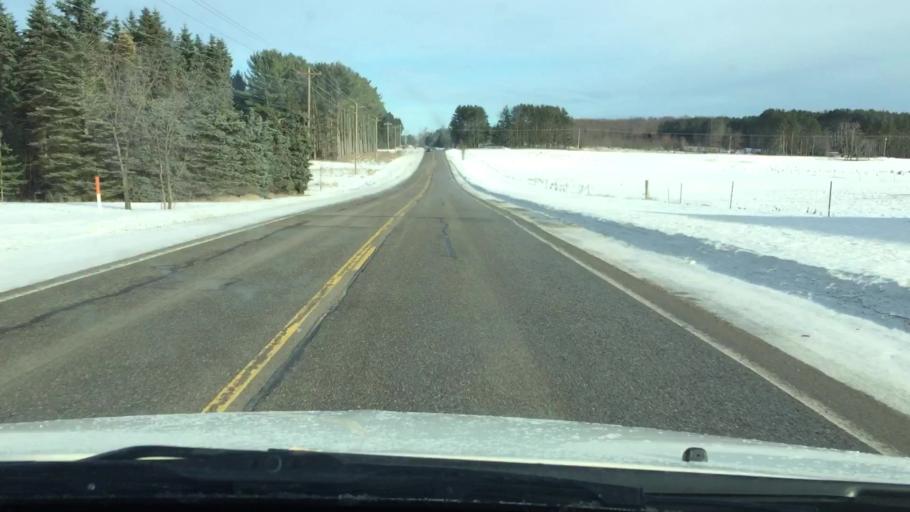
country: US
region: Michigan
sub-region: Kalkaska County
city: Kalkaska
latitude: 44.6409
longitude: -85.2561
